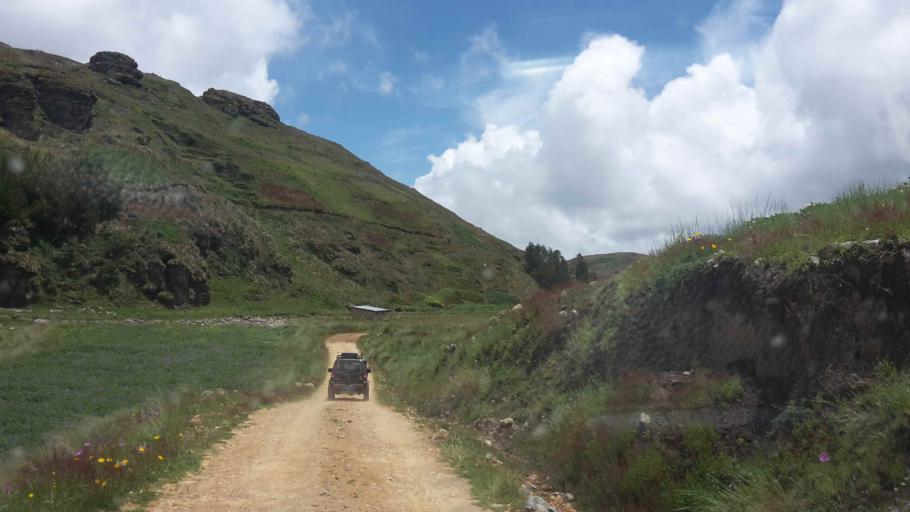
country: BO
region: Cochabamba
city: Cochabamba
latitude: -17.1857
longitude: -66.0682
